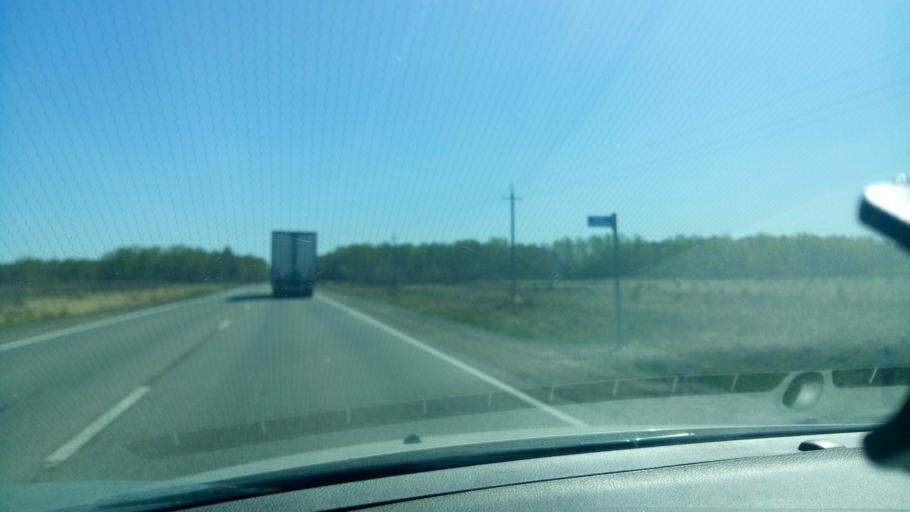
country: RU
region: Sverdlovsk
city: Bogdanovich
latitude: 56.7535
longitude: 62.1522
